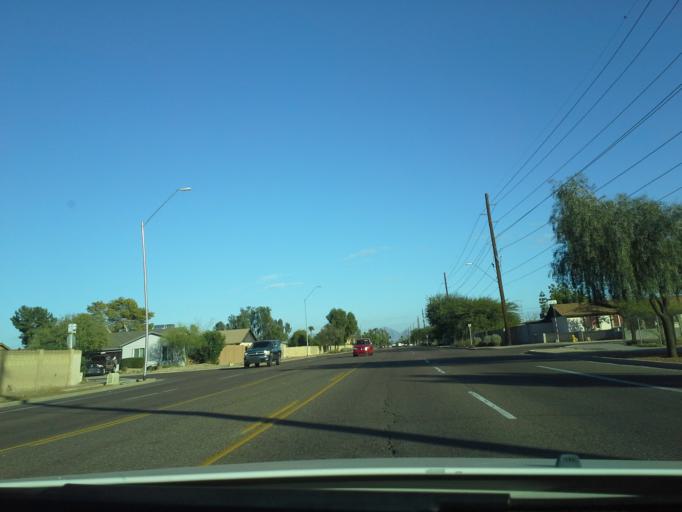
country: US
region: Arizona
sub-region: Maricopa County
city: Glendale
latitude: 33.6546
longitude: -112.0879
